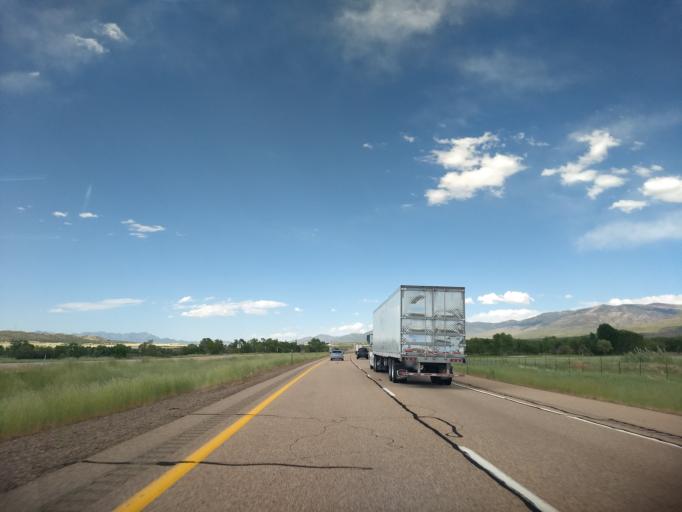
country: US
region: Utah
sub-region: Millard County
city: Fillmore
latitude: 38.9828
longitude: -112.3341
